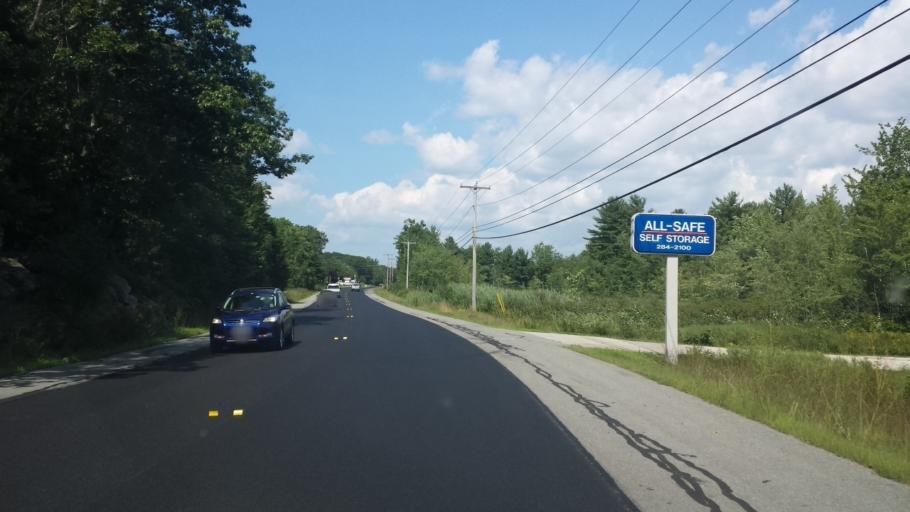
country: US
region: Maine
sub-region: York County
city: Arundel
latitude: 43.4366
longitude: -70.5041
